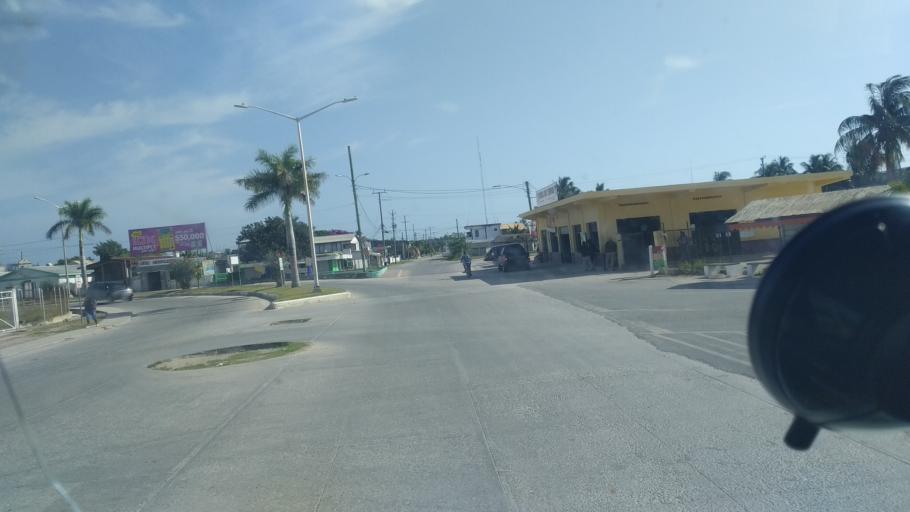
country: BZ
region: Corozal
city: Corozal
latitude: 18.3927
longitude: -88.3886
